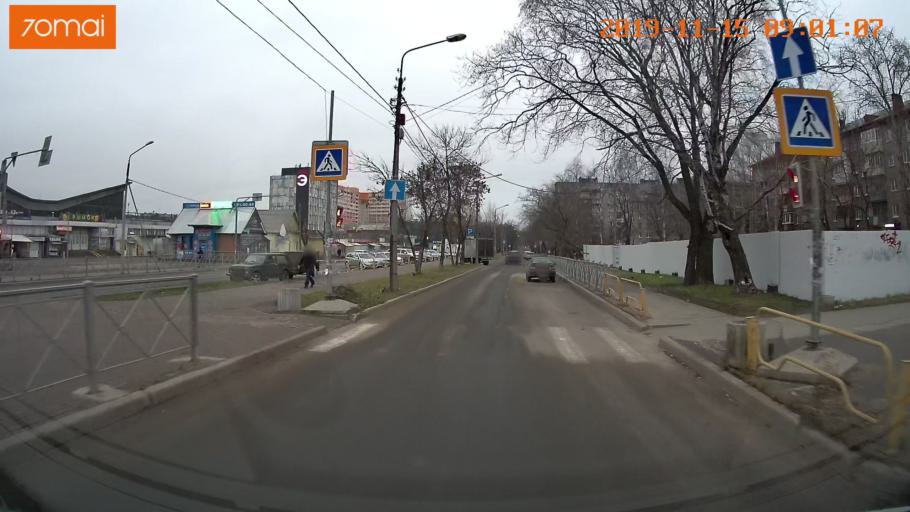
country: RU
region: Vologda
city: Cherepovets
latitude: 59.1306
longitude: 37.9251
